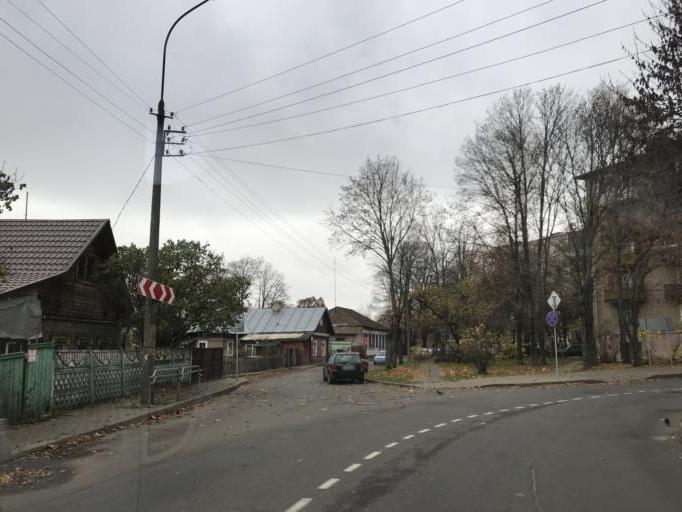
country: BY
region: Mogilev
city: Mahilyow
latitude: 53.9028
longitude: 30.3459
